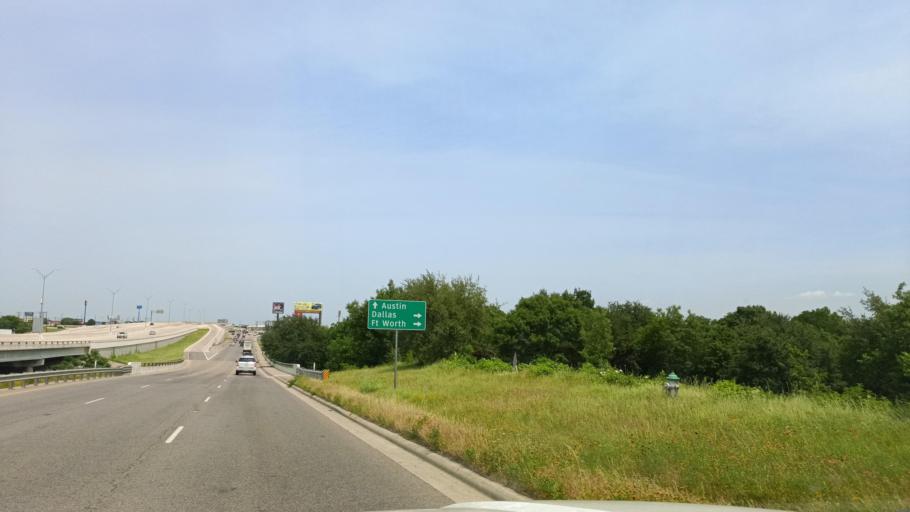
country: US
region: Texas
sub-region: Bell County
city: Temple
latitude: 31.0854
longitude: -97.3844
